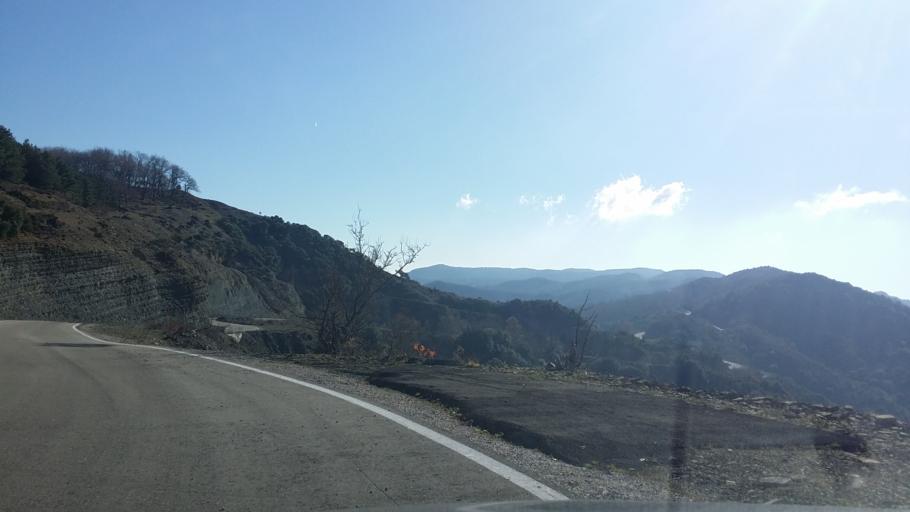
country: GR
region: West Greece
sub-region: Nomos Aitolias kai Akarnanias
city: Krikellos
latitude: 38.9968
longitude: 21.2771
